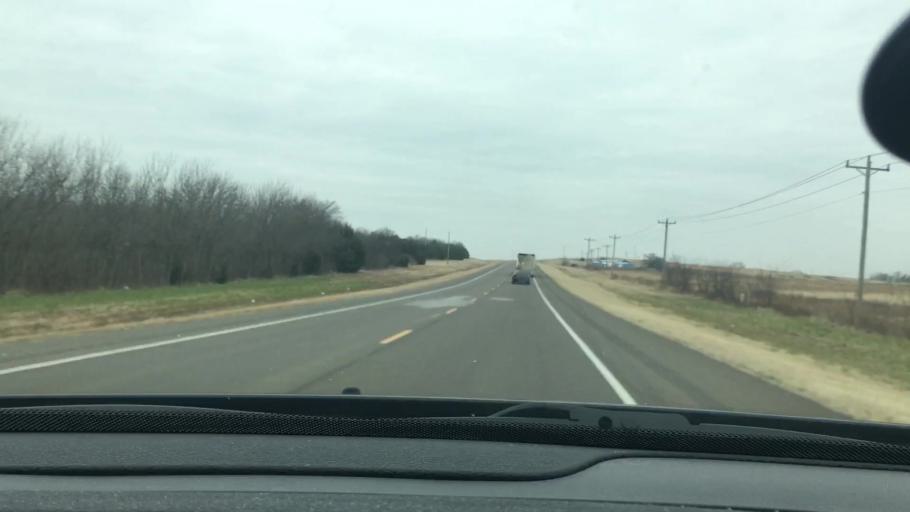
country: US
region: Oklahoma
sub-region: Murray County
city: Davis
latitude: 34.5167
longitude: -97.2059
